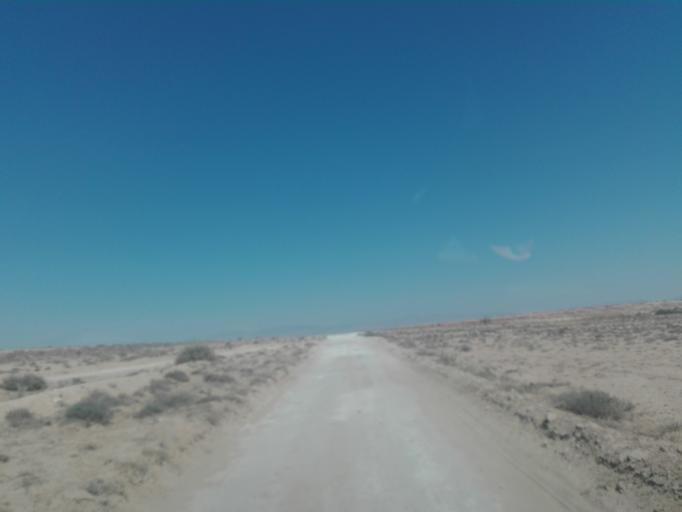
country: TN
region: Safaqis
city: Skhira
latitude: 34.3114
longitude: 9.9125
